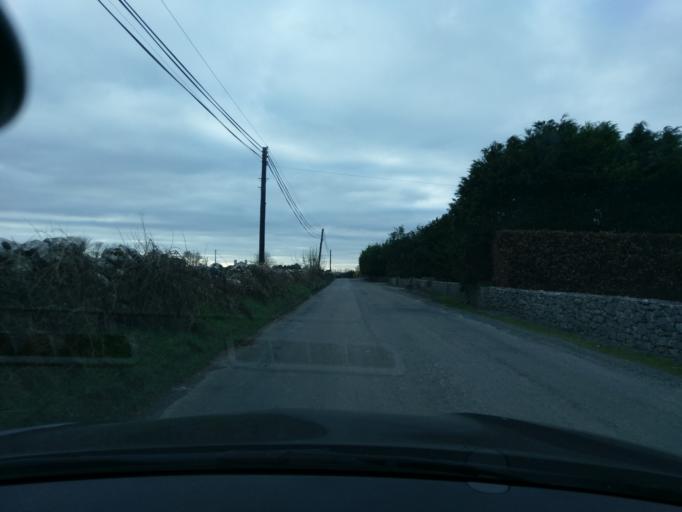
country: IE
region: Connaught
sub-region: County Galway
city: Oranmore
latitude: 53.2096
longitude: -8.8529
